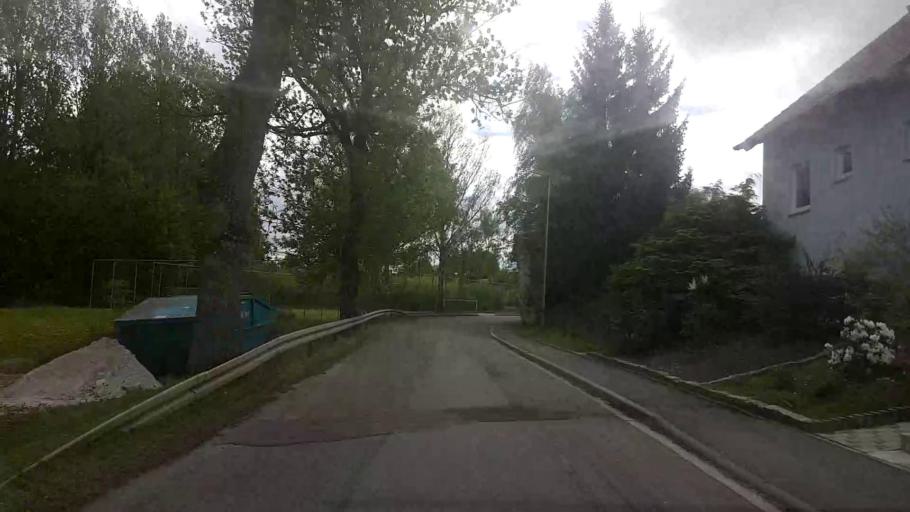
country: DE
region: Bavaria
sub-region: Upper Franconia
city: Untersiemau
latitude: 50.1849
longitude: 10.9958
